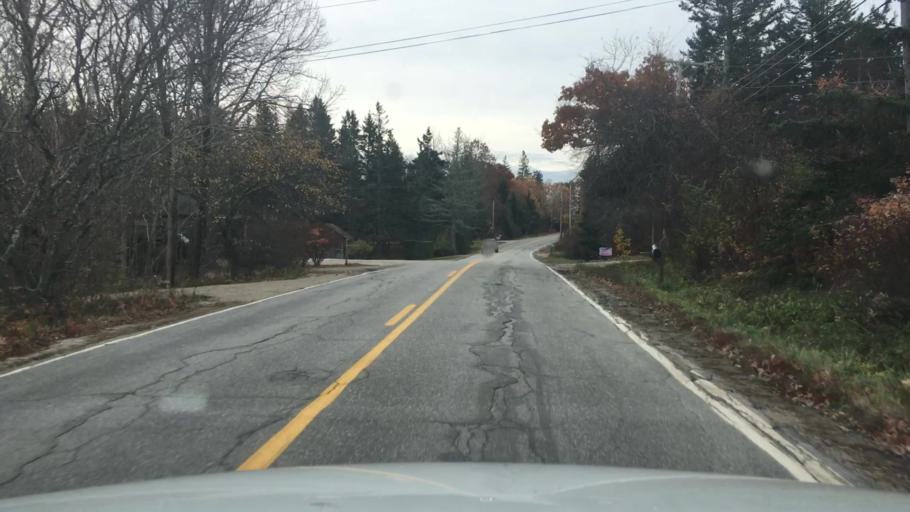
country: US
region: Maine
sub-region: Hancock County
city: Sedgwick
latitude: 44.3582
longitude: -68.5493
